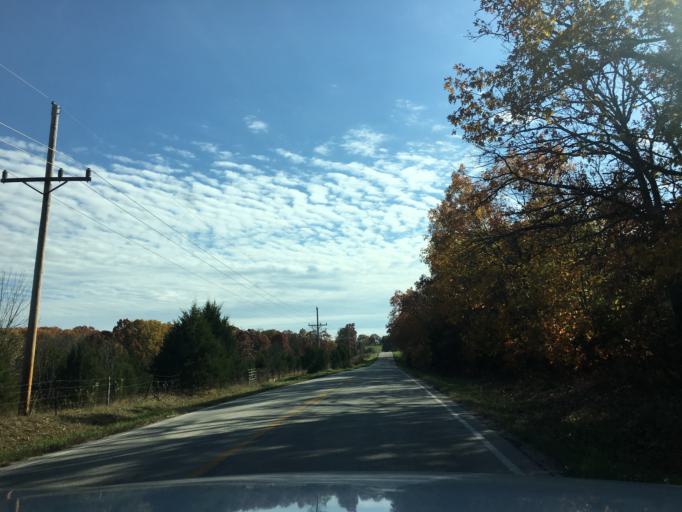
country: US
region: Missouri
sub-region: Maries County
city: Belle
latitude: 38.3305
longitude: -91.7620
